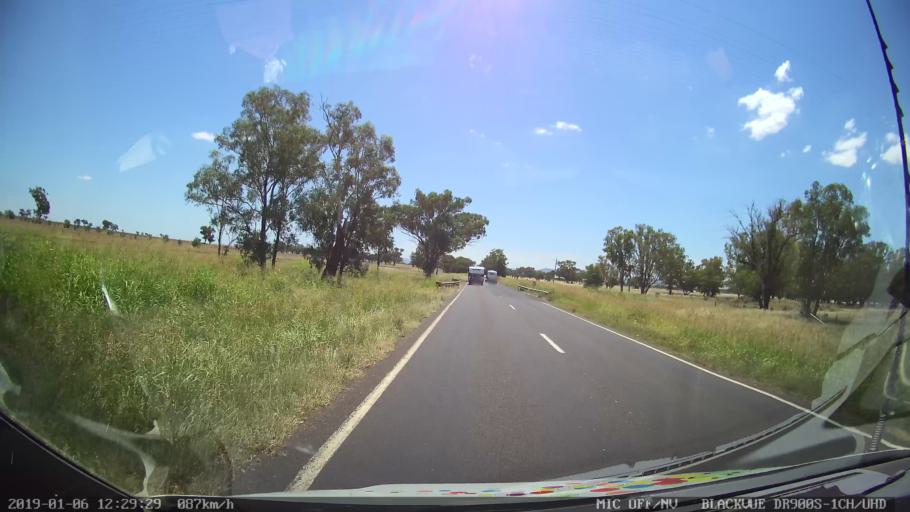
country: AU
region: New South Wales
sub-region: Tamworth Municipality
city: Phillip
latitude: -31.1841
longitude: 150.8447
